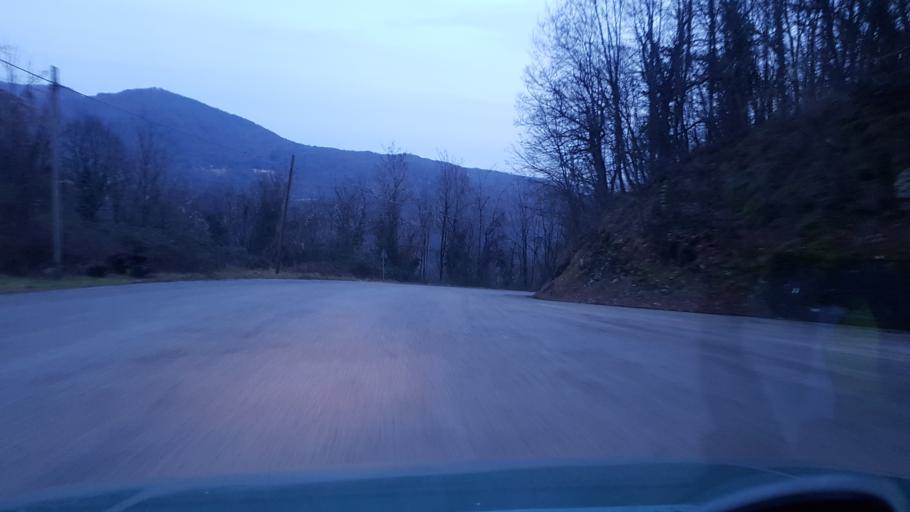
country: IT
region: Friuli Venezia Giulia
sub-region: Provincia di Udine
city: Pulfero
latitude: 46.1558
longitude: 13.4739
